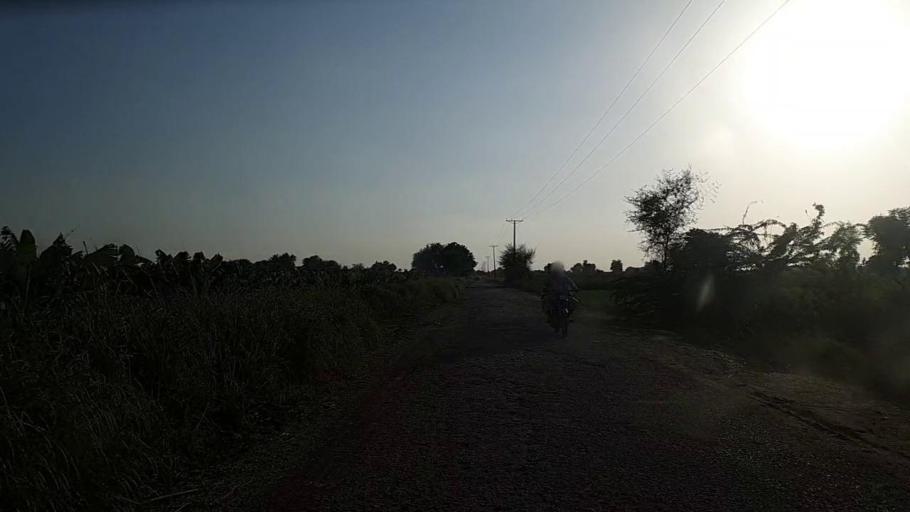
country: PK
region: Sindh
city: Hingorja
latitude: 27.0601
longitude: 68.4159
